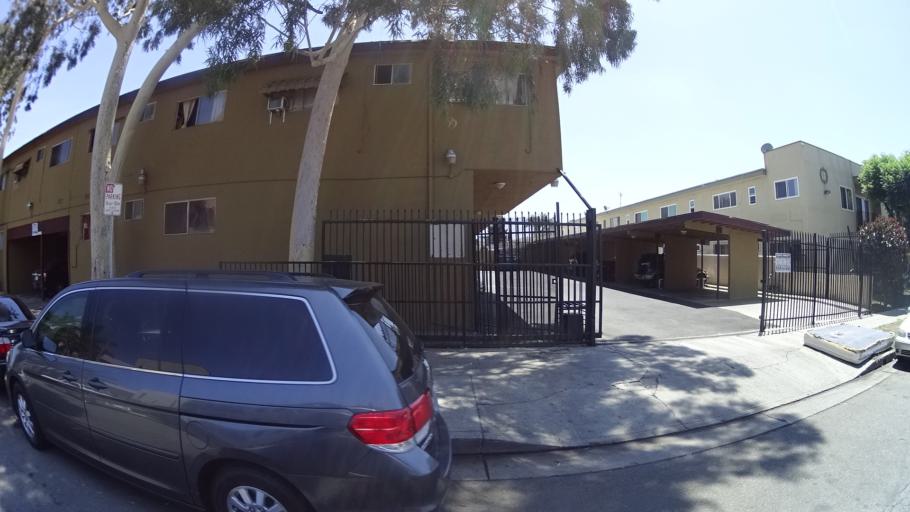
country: US
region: California
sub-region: Los Angeles County
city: Van Nuys
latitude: 34.2312
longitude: -118.4536
